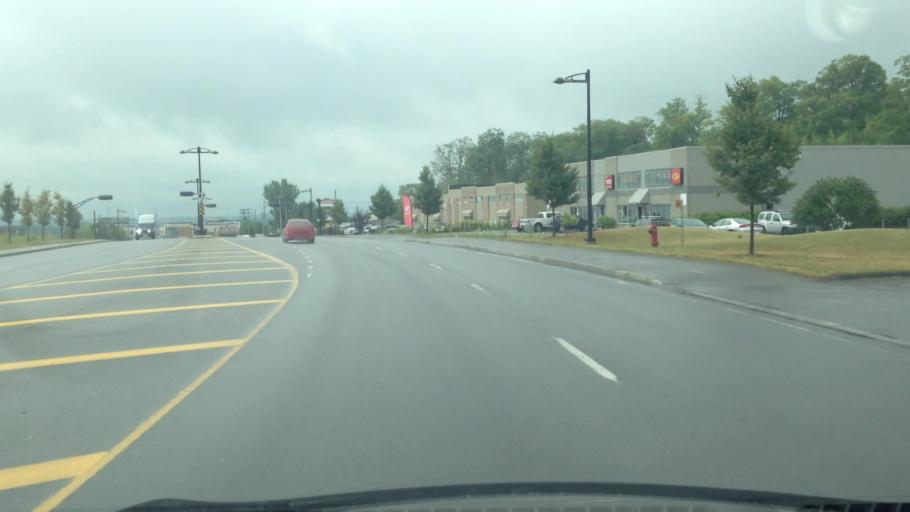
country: CA
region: Quebec
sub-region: Laurentides
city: Saint-Jerome
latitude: 45.7587
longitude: -74.0246
